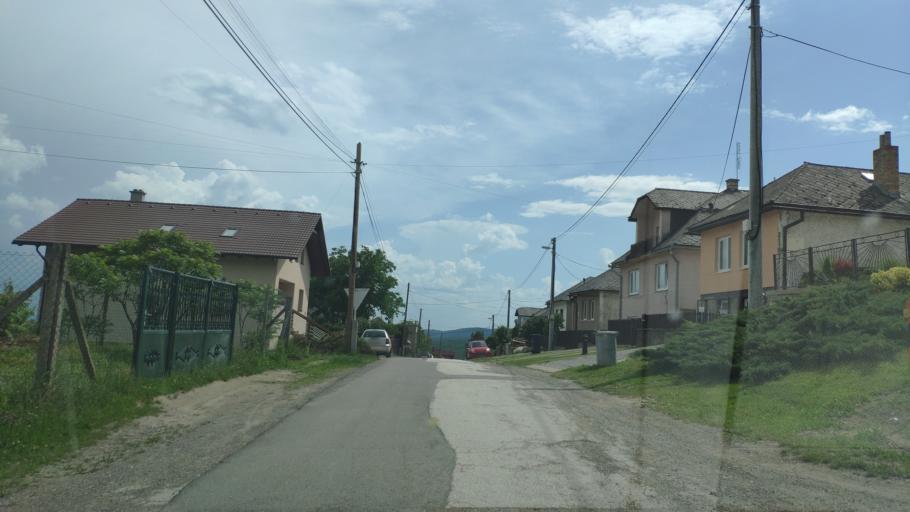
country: SK
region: Kosicky
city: Medzev
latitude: 48.7141
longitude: 20.9740
